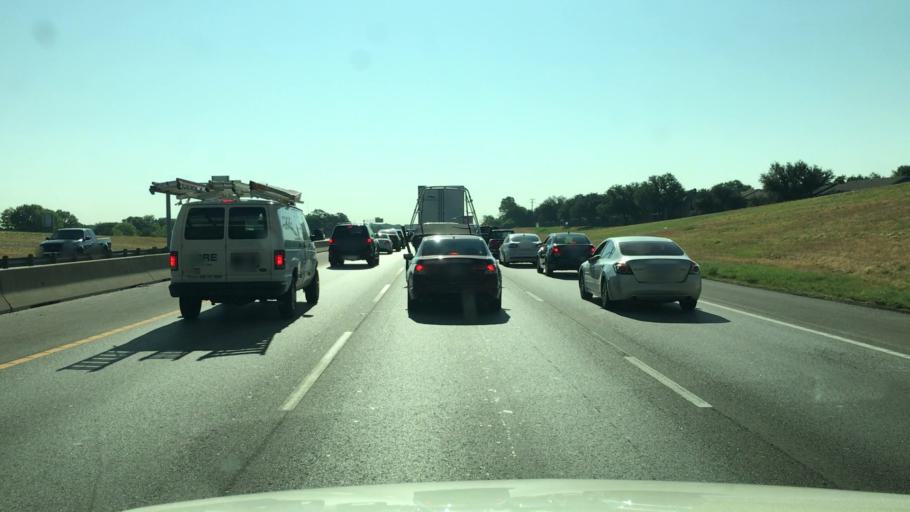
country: US
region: Texas
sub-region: Tarrant County
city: Pantego
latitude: 32.7601
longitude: -97.1672
